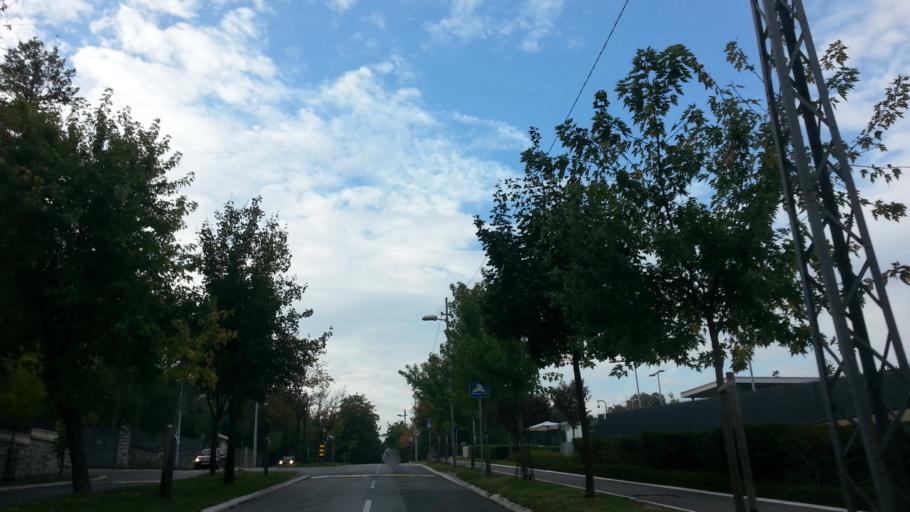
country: RS
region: Central Serbia
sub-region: Belgrade
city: Savski Venac
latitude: 44.7724
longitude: 20.4546
